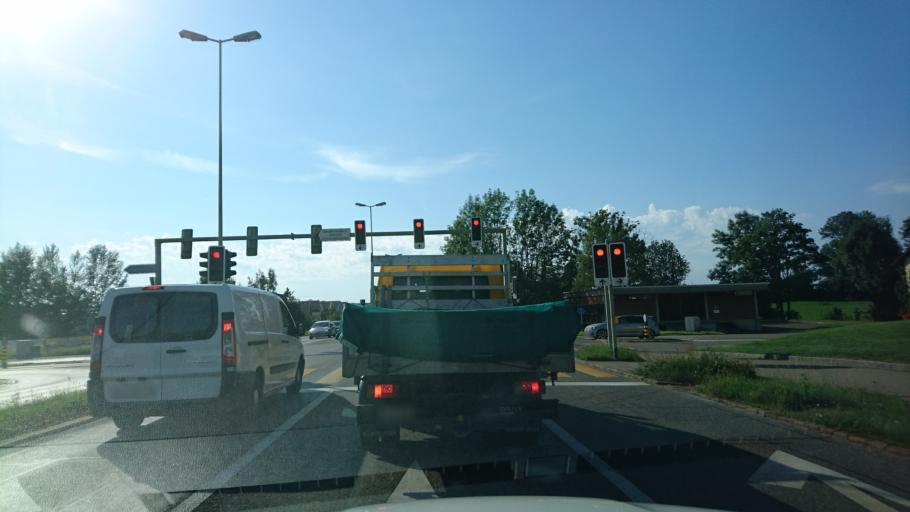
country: CH
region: Zurich
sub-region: Bezirk Hinwil
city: Hinwil
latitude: 47.3047
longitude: 8.8293
